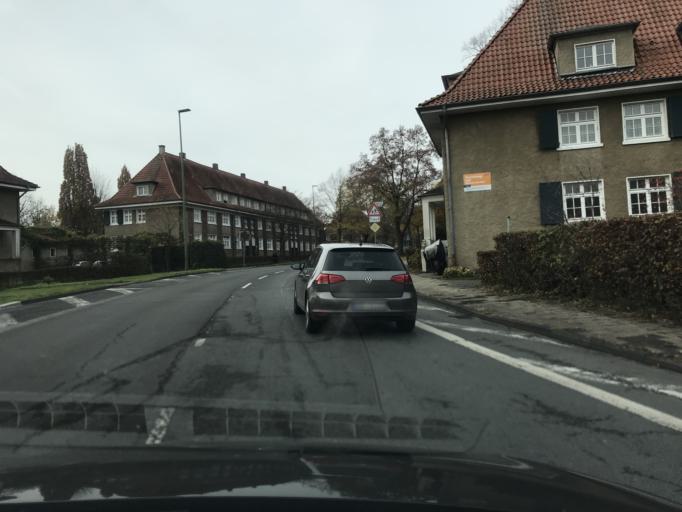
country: DE
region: North Rhine-Westphalia
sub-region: Regierungsbezirk Arnsberg
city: Hamm
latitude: 51.7058
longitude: 7.8142
